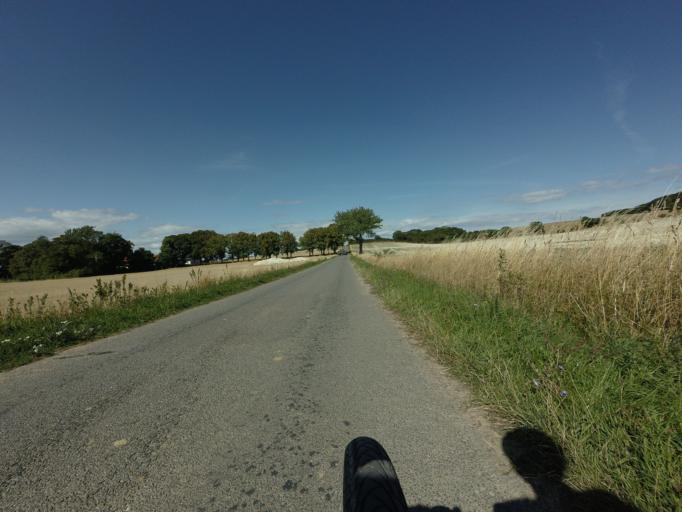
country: DK
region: Zealand
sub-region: Vordingborg Kommune
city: Stege
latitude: 55.0130
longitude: 12.4598
